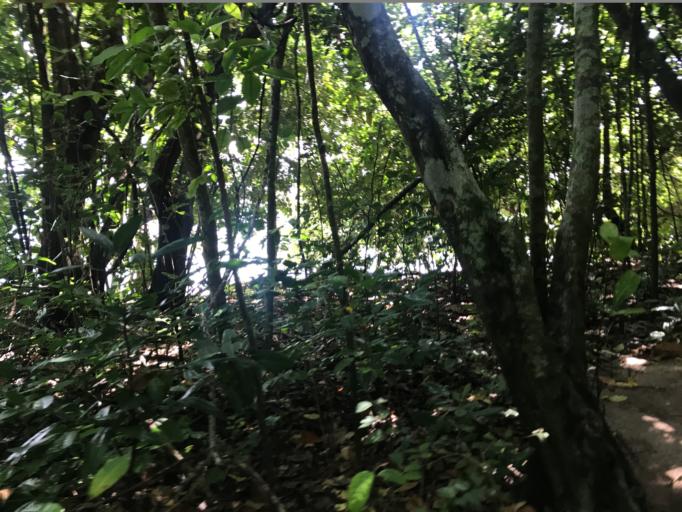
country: AU
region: Queensland
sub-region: Cairns
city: Yorkeys Knob
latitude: -16.7592
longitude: 145.9754
